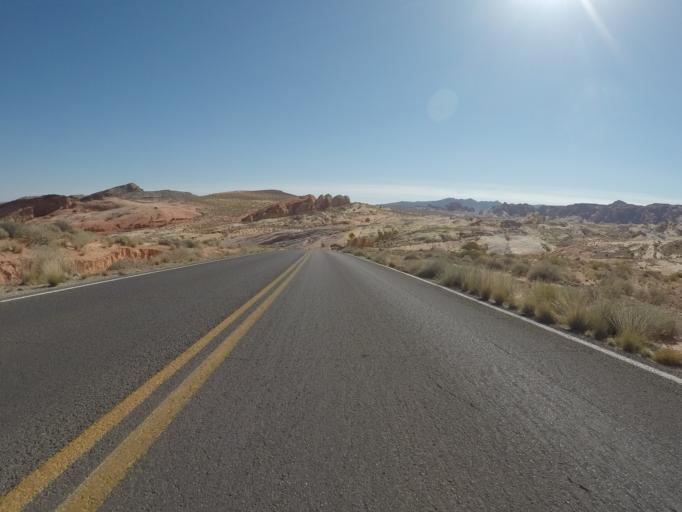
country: US
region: Nevada
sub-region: Clark County
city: Moapa Valley
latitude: 36.4826
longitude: -114.5266
